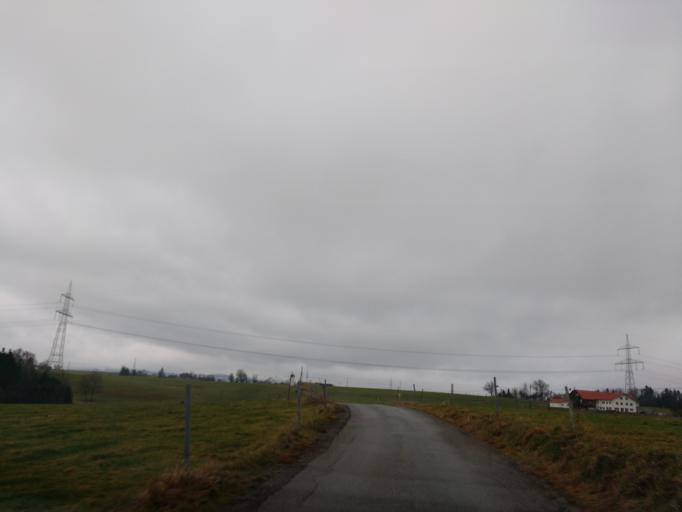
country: DE
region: Bavaria
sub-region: Swabia
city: Neuburg
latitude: 47.7588
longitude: 10.3677
